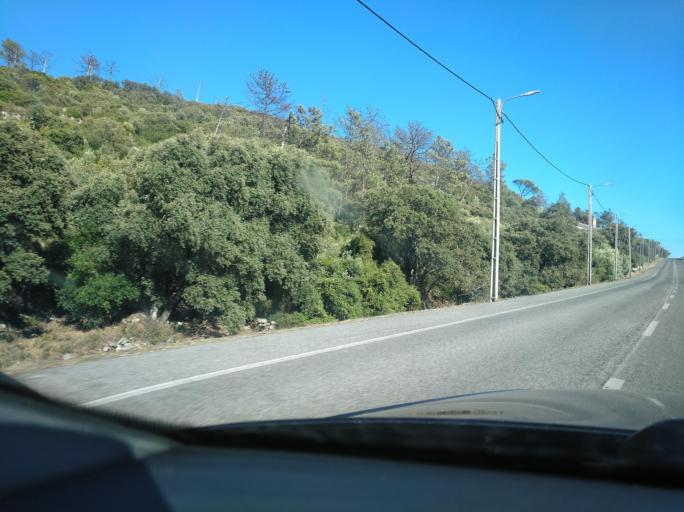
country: PT
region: Santarem
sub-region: Alcanena
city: Alcanena
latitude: 39.5088
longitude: -8.6811
